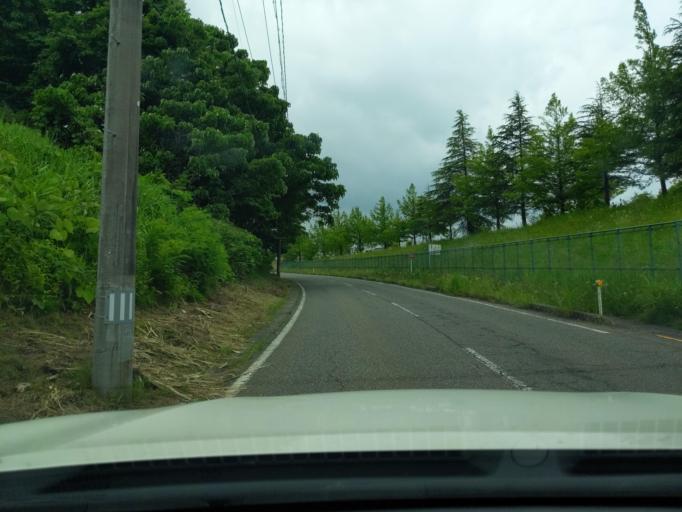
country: JP
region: Niigata
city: Kashiwazaki
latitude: 37.3453
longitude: 138.6034
